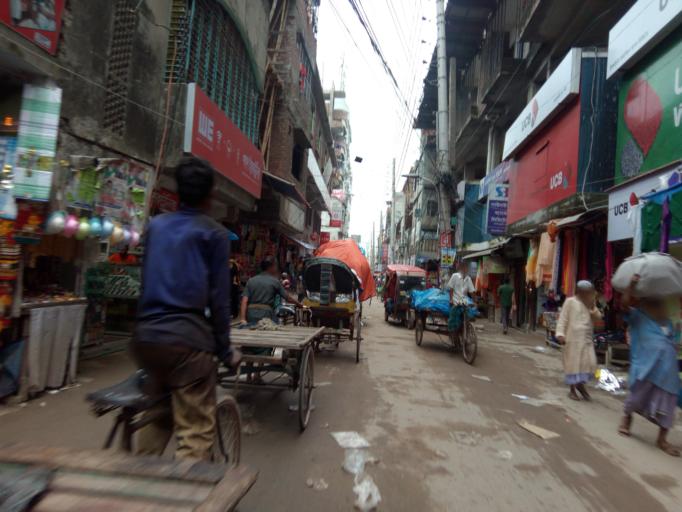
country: BD
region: Dhaka
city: Azimpur
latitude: 23.7202
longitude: 90.3738
